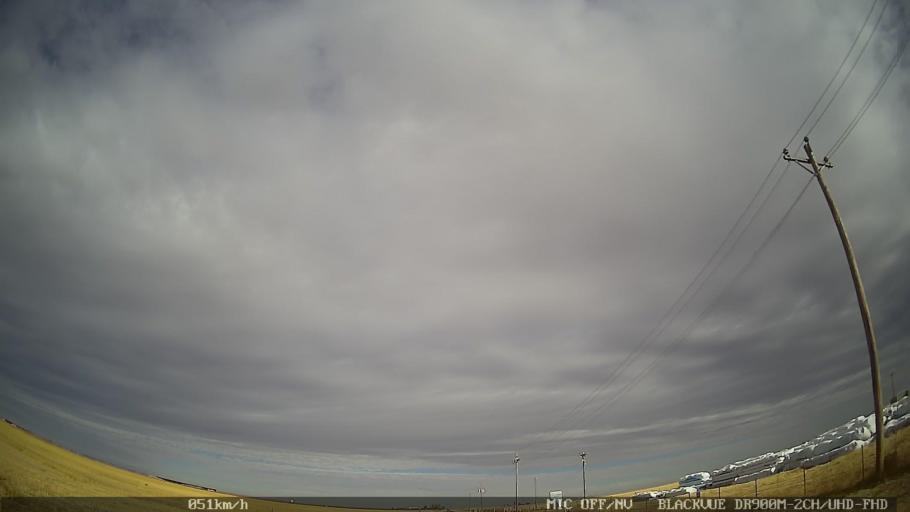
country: US
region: New Mexico
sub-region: Curry County
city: Texico
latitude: 34.4259
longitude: -103.0907
